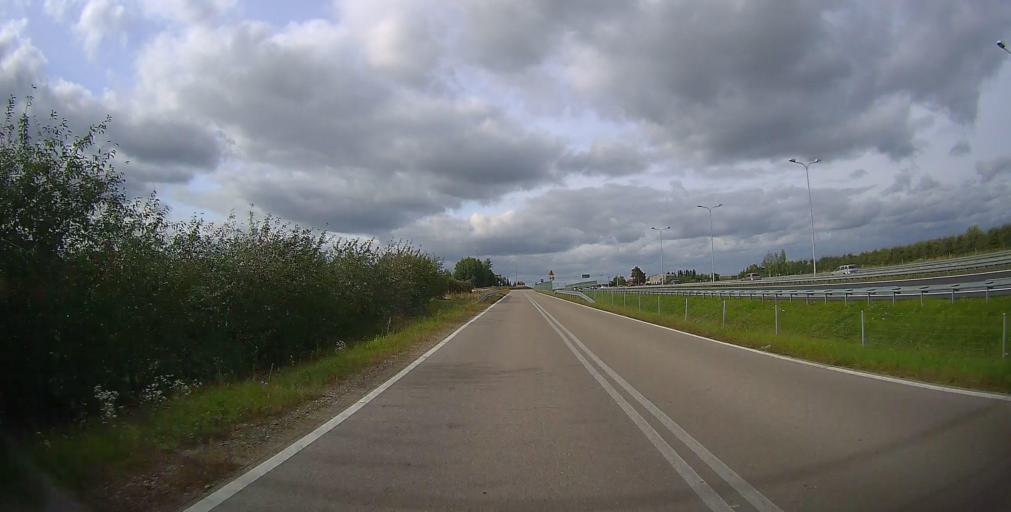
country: PL
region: Masovian Voivodeship
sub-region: Powiat grojecki
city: Goszczyn
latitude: 51.7500
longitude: 20.9067
